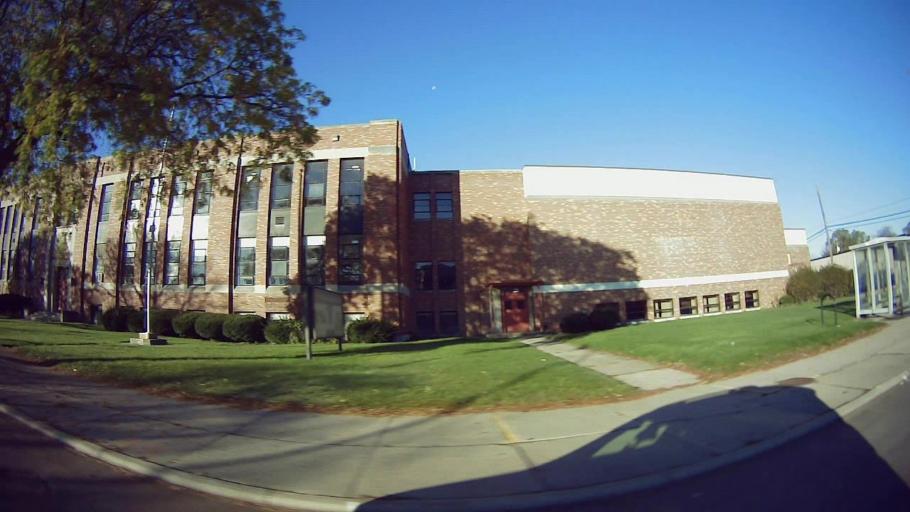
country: US
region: Michigan
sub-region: Oakland County
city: Berkley
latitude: 42.4931
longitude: -83.1836
